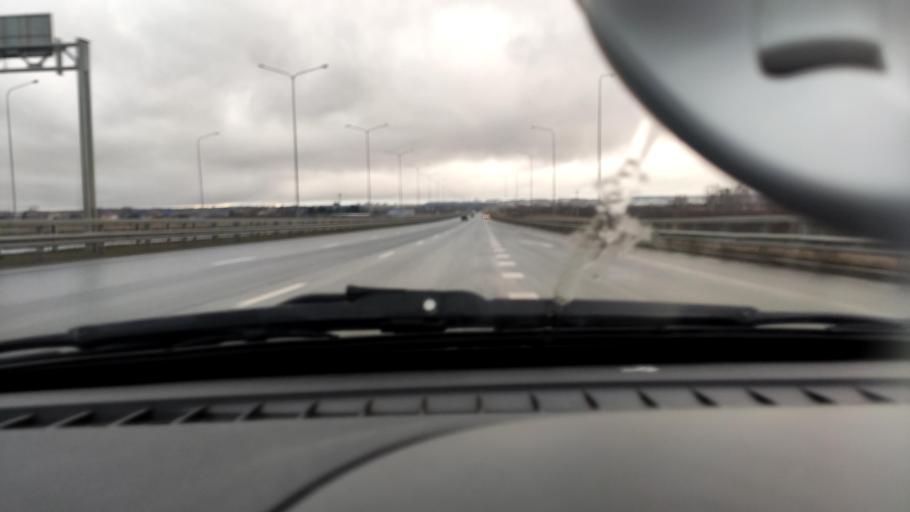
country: RU
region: Perm
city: Froly
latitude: 57.8836
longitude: 56.2675
